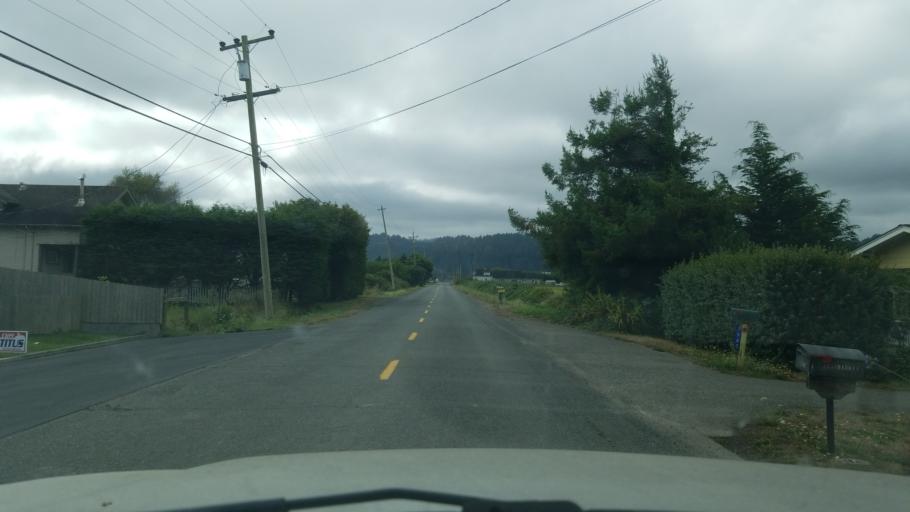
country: US
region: California
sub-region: Humboldt County
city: Ferndale
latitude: 40.5933
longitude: -124.2553
